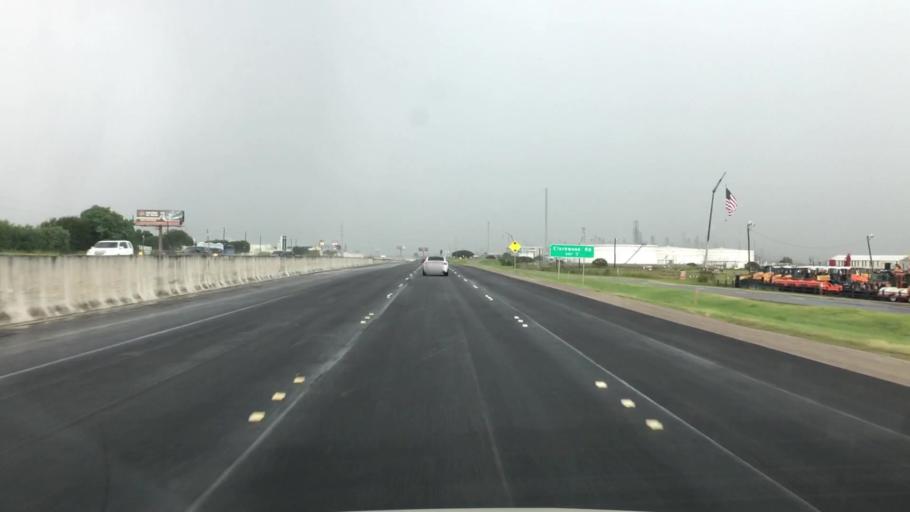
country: US
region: Texas
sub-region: Nueces County
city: Corpus Christi
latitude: 27.8155
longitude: -97.5104
